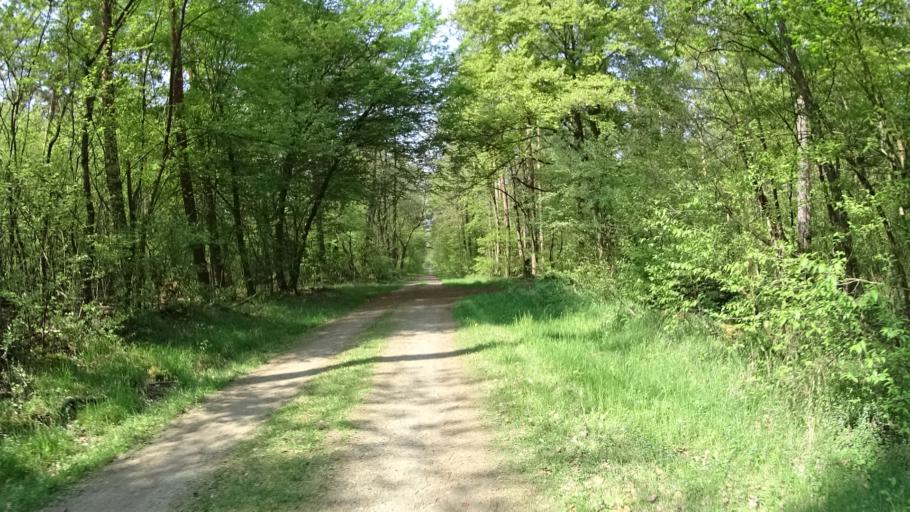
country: DE
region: Hesse
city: Lampertheim
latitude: 49.5609
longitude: 8.4996
